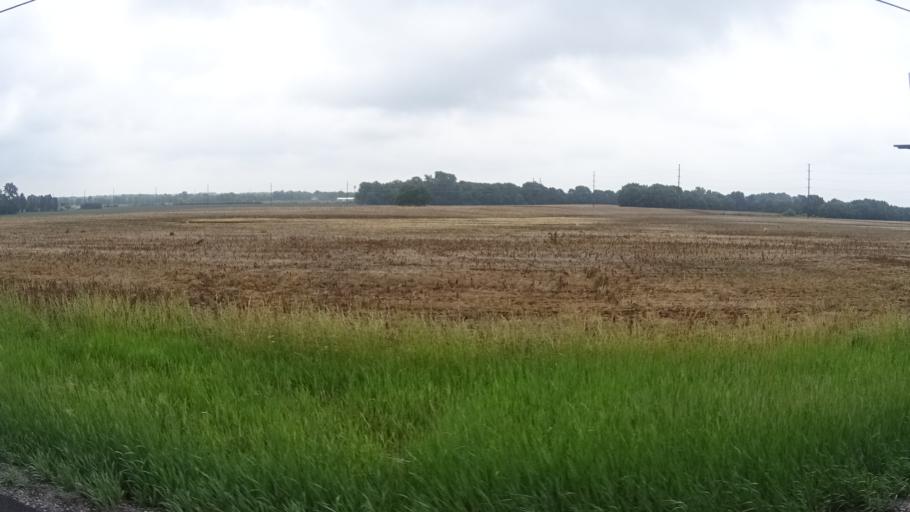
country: US
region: Ohio
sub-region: Erie County
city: Sandusky
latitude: 41.3559
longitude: -82.7519
